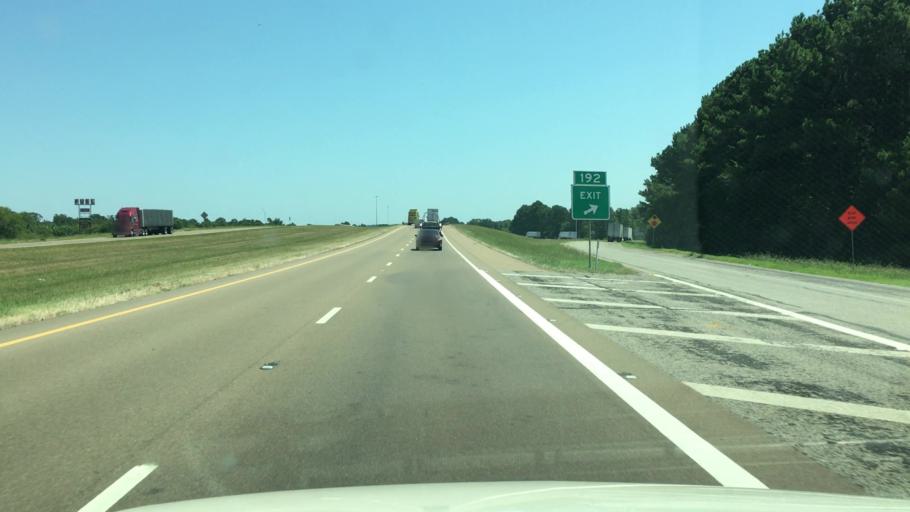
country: US
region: Texas
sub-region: Bowie County
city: De Kalb
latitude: 33.4129
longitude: -94.5610
